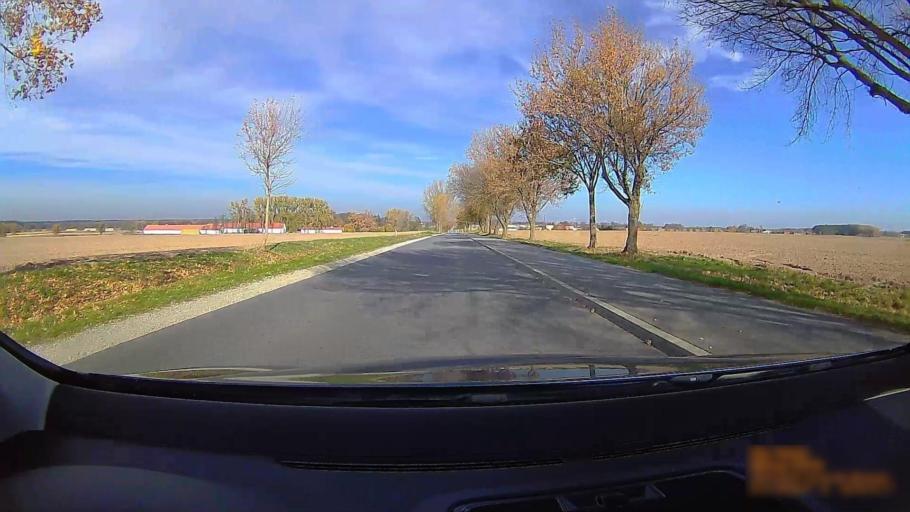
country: PL
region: Greater Poland Voivodeship
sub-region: Powiat kepinski
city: Kepno
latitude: 51.3394
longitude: 18.0216
